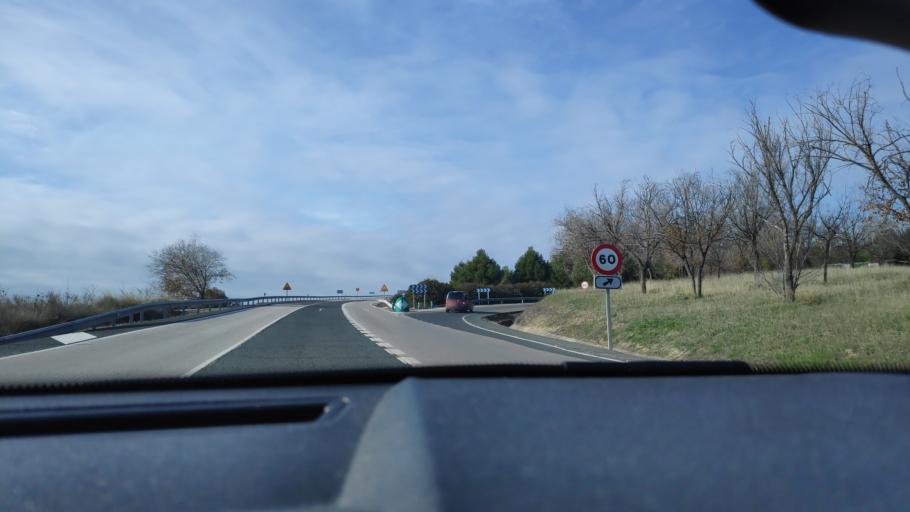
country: ES
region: Andalusia
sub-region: Provincia de Jaen
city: Linares
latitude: 38.0782
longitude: -3.6083
